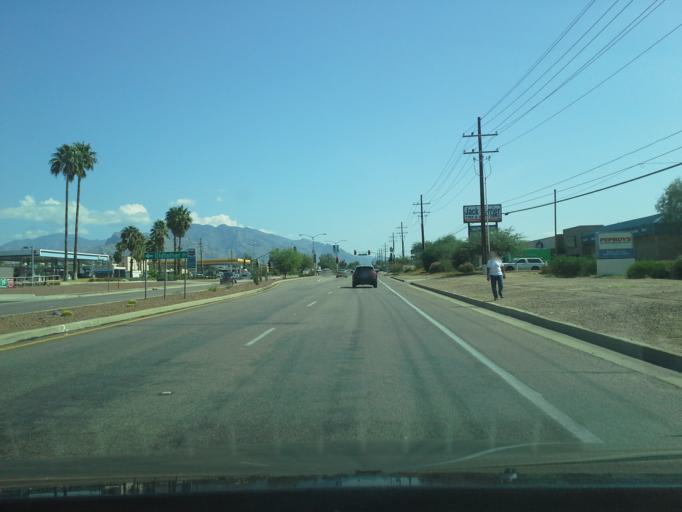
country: US
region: Arizona
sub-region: Pima County
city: Casas Adobes
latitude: 32.3375
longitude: -111.0573
